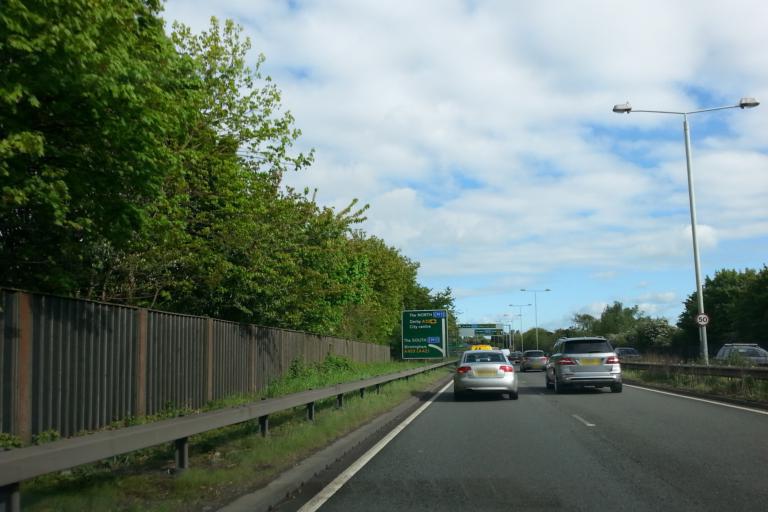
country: GB
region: England
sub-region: Nottinghamshire
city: Ruddington
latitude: 52.9182
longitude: -1.1621
